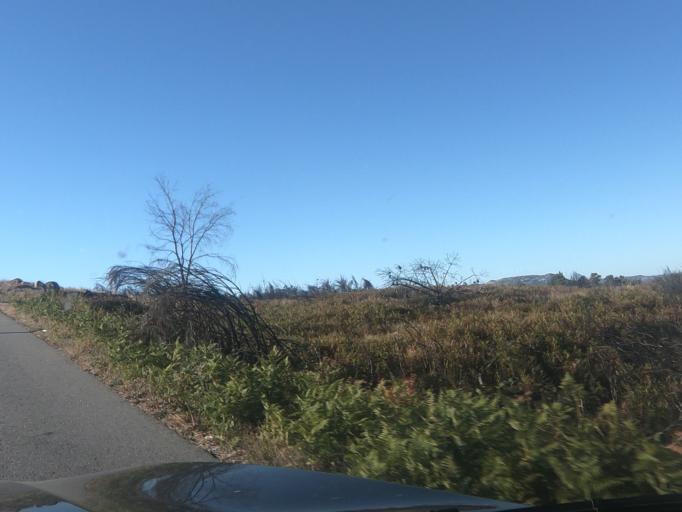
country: PT
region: Vila Real
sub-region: Sabrosa
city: Sabrosa
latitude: 41.3266
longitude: -7.6143
